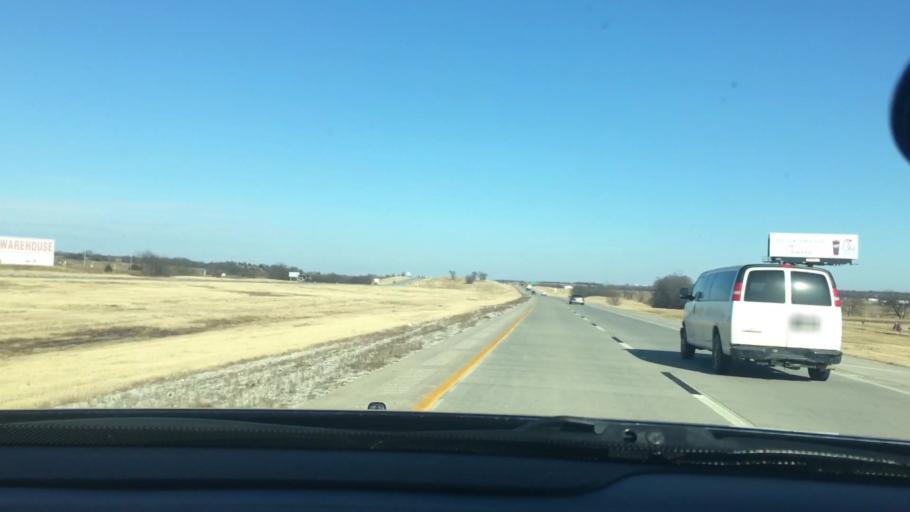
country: US
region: Oklahoma
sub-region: Carter County
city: Ardmore
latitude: 34.0759
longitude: -97.1494
